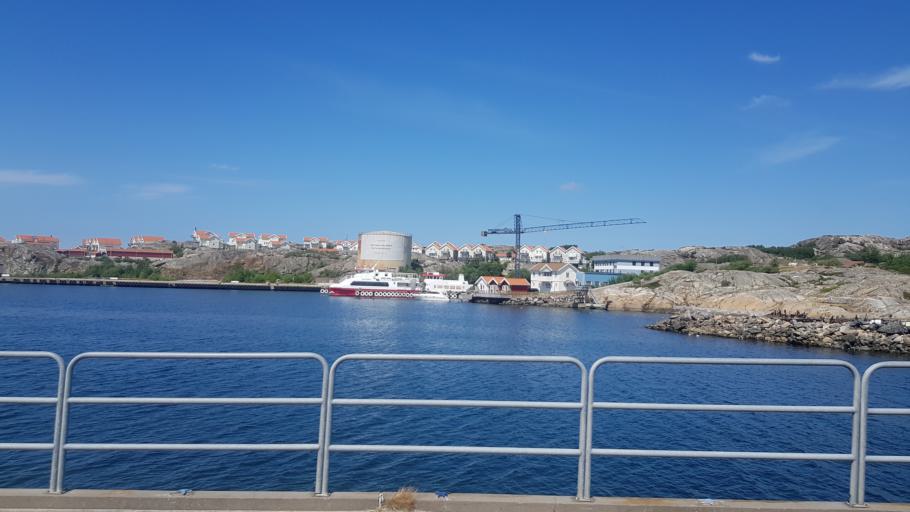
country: SE
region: Vaestra Goetaland
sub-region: Tjorns Kommun
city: Skaerhamn
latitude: 57.9931
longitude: 11.5469
